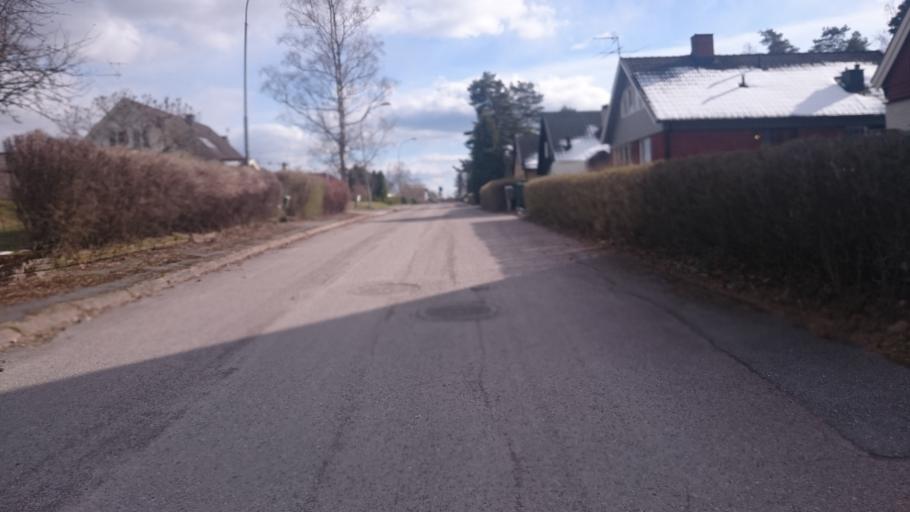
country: SE
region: OErebro
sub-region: Karlskoga Kommun
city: Karlskoga
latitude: 59.3074
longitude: 14.4922
